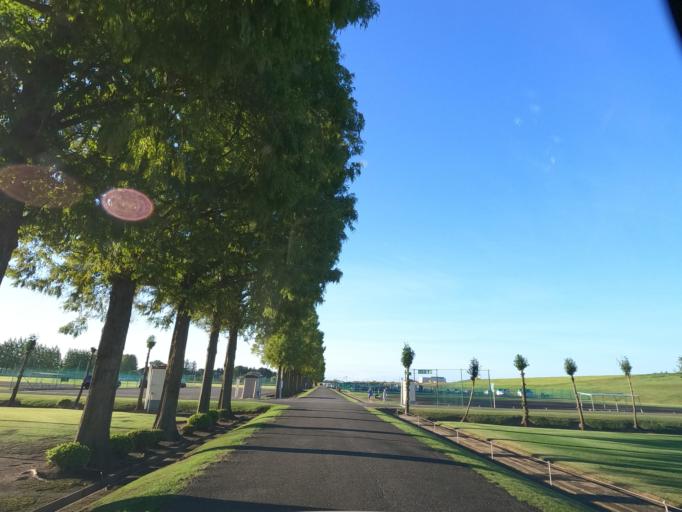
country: JP
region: Saitama
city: Shiki
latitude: 35.8891
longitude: 139.5763
